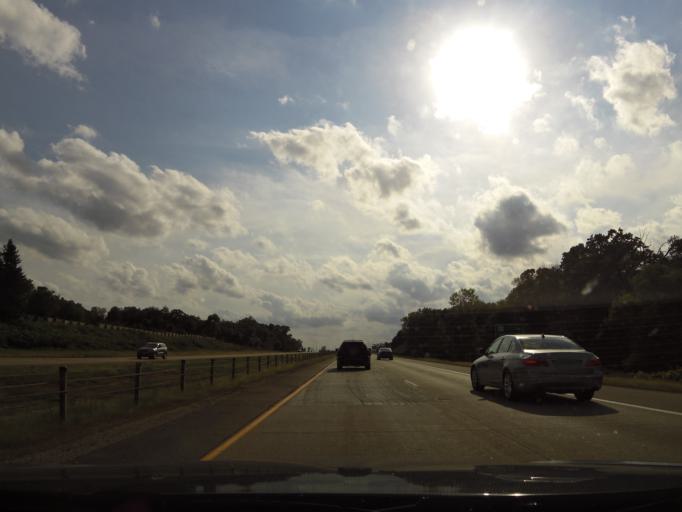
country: US
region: Minnesota
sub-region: Dakota County
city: Apple Valley
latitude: 44.7651
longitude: -93.2385
